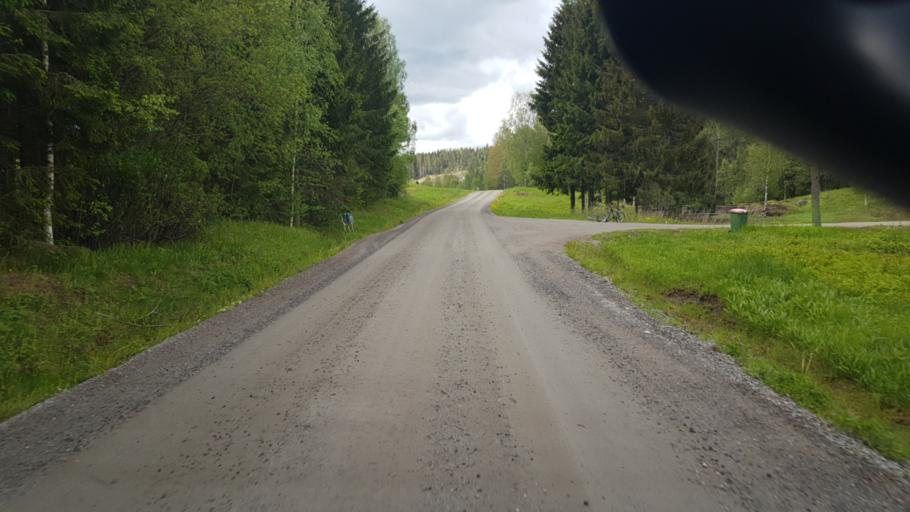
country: NO
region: Ostfold
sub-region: Romskog
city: Romskog
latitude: 59.6862
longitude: 11.9341
